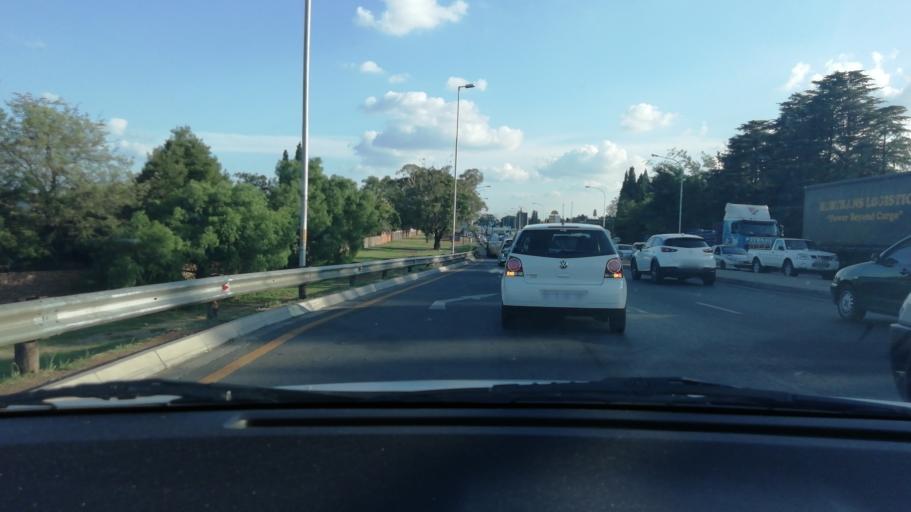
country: ZA
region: Gauteng
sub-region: Ekurhuleni Metropolitan Municipality
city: Boksburg
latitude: -26.1751
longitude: 28.2803
